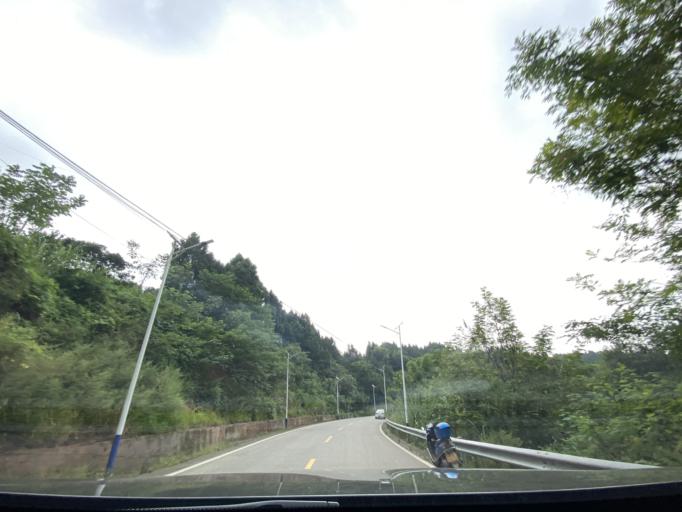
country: CN
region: Sichuan
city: Jiancheng
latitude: 30.5531
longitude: 104.5213
